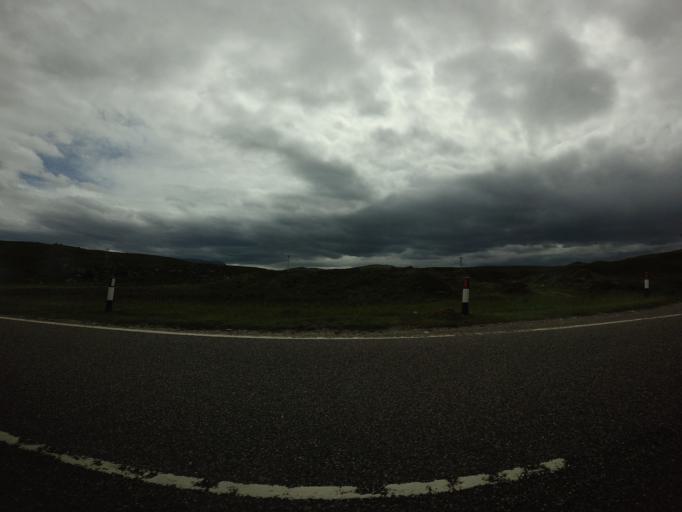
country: GB
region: Scotland
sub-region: Highland
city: Dingwall
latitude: 57.6937
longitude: -4.7392
